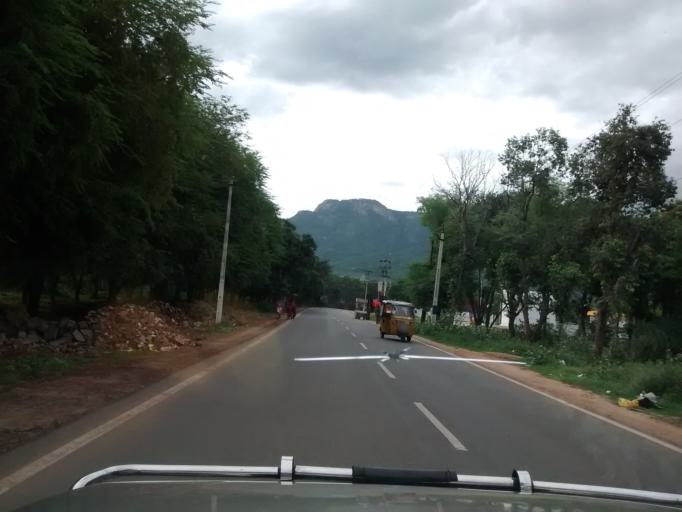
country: IN
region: Andhra Pradesh
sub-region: Chittoor
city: Narasingapuram
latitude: 13.6171
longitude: 79.3631
